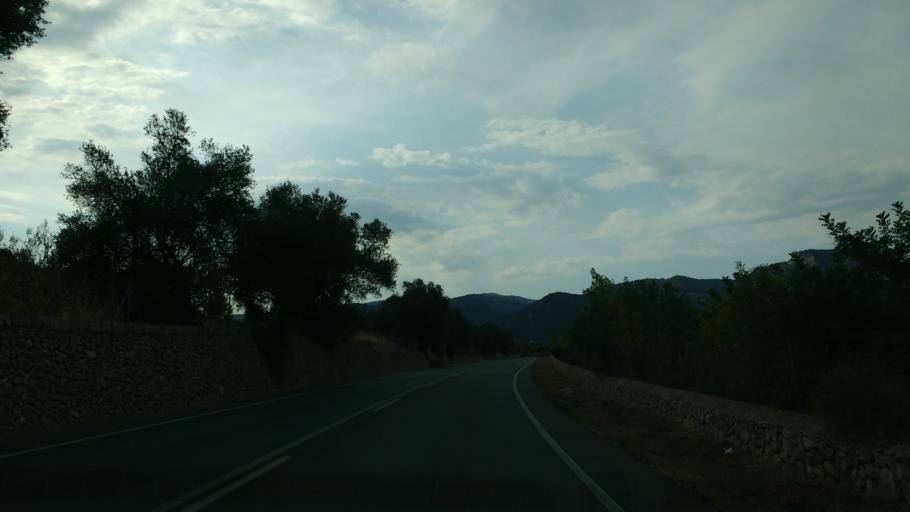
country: ES
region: Balearic Islands
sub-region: Illes Balears
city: Consell
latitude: 39.6867
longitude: 2.8085
